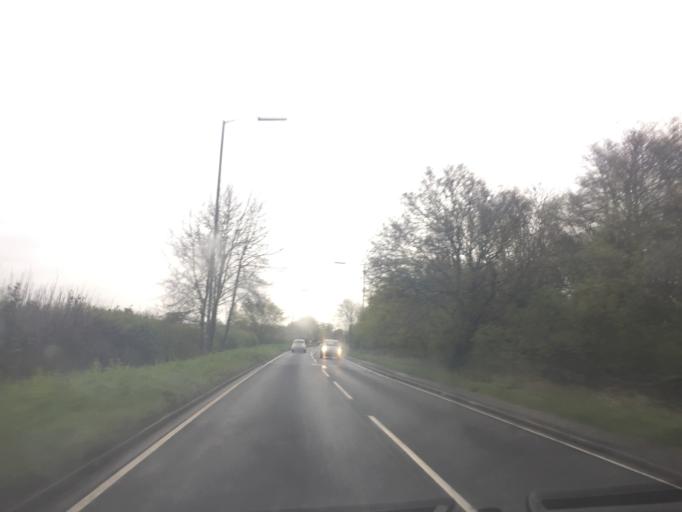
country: GB
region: England
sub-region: Essex
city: Epping
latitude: 51.7165
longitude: 0.1277
